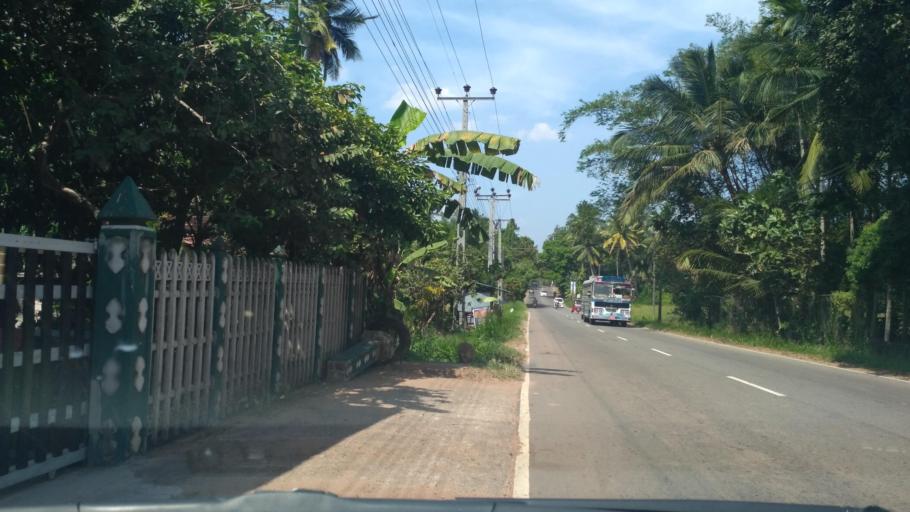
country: LK
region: North Western
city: Kuliyapitiya
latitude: 7.3633
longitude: 80.0340
